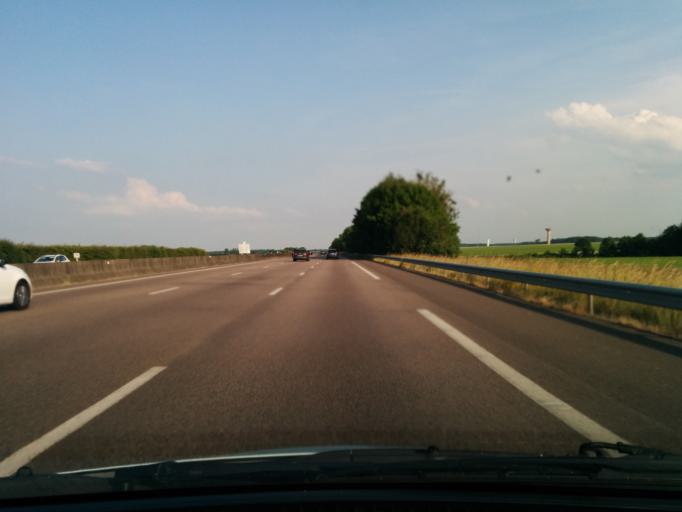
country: FR
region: Haute-Normandie
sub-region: Departement de l'Eure
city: Houlbec-Cocherel
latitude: 49.1009
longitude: 1.3514
